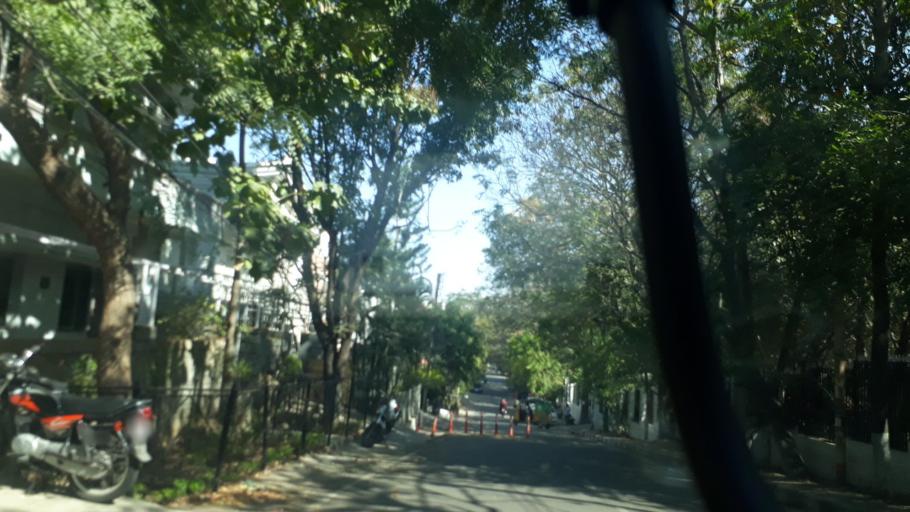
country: IN
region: Telangana
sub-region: Rangareddi
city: Kukatpalli
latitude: 17.4223
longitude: 78.3998
